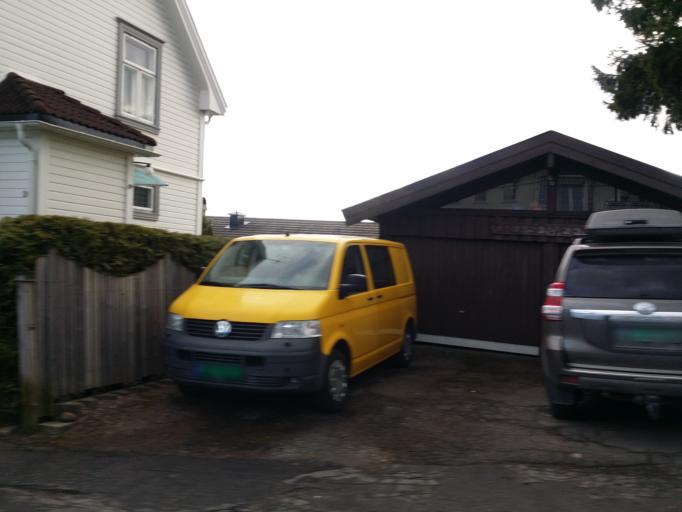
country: NO
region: Oslo
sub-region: Oslo
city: Oslo
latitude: 59.9507
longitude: 10.7889
